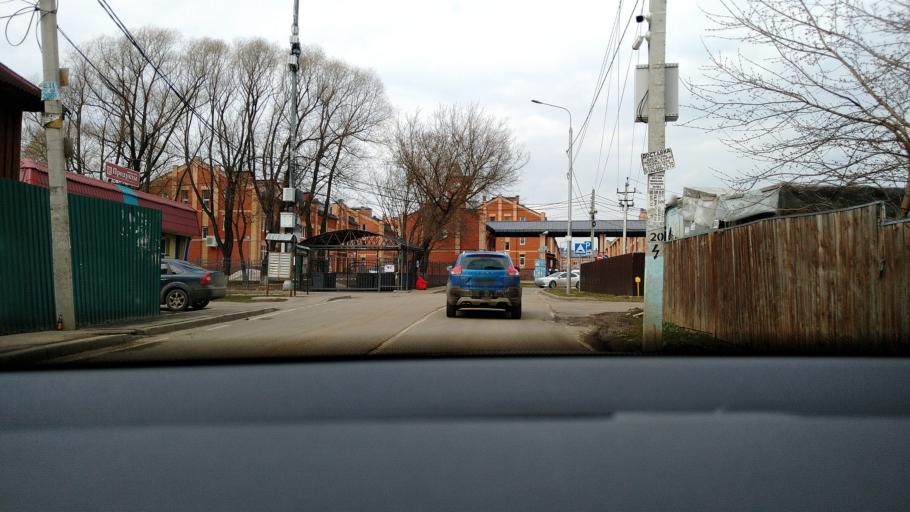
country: RU
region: Moskovskaya
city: Mosrentgen
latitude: 55.5947
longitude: 37.4433
